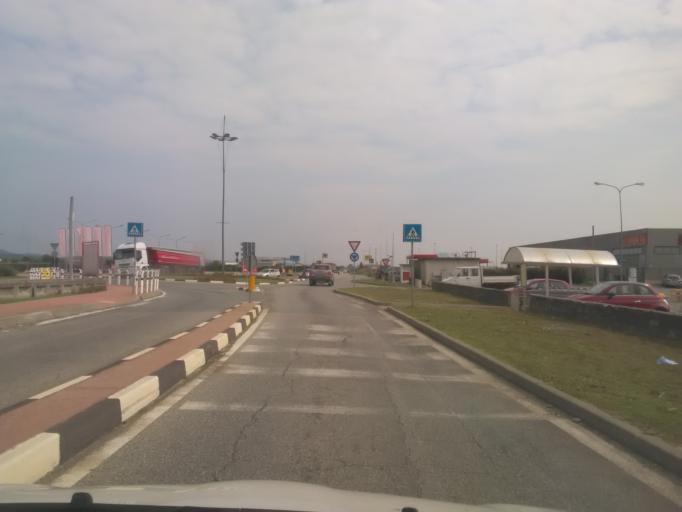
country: IT
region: Piedmont
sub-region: Provincia di Vercelli
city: Cigliano
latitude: 45.3186
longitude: 8.0306
